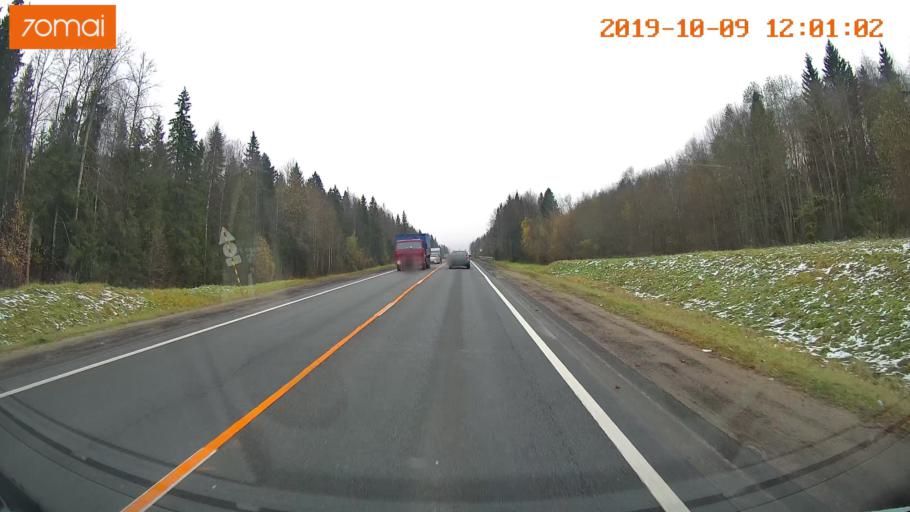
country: RU
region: Vologda
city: Gryazovets
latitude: 58.6925
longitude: 40.3015
